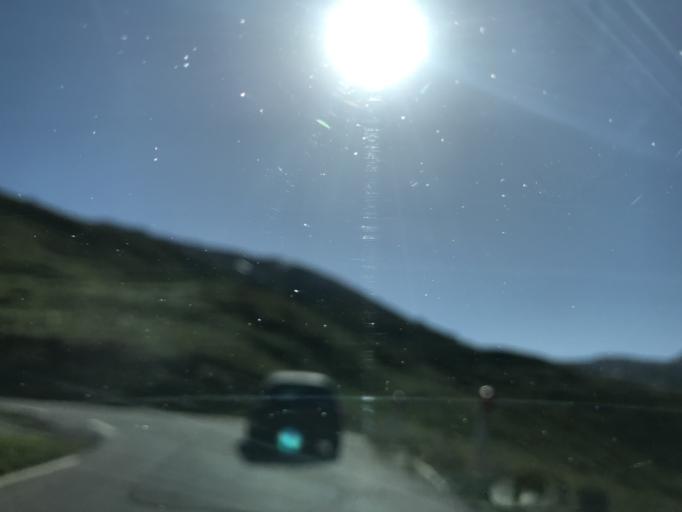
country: IT
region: Piedmont
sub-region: Provincia di Cuneo
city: Pontechianale
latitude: 44.6959
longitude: 6.9514
